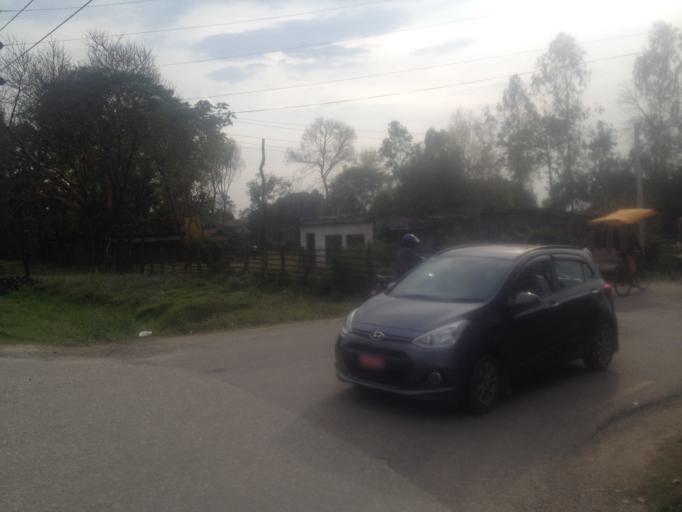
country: NP
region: Central Region
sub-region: Narayani Zone
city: Bharatpur
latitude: 27.6919
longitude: 84.4403
